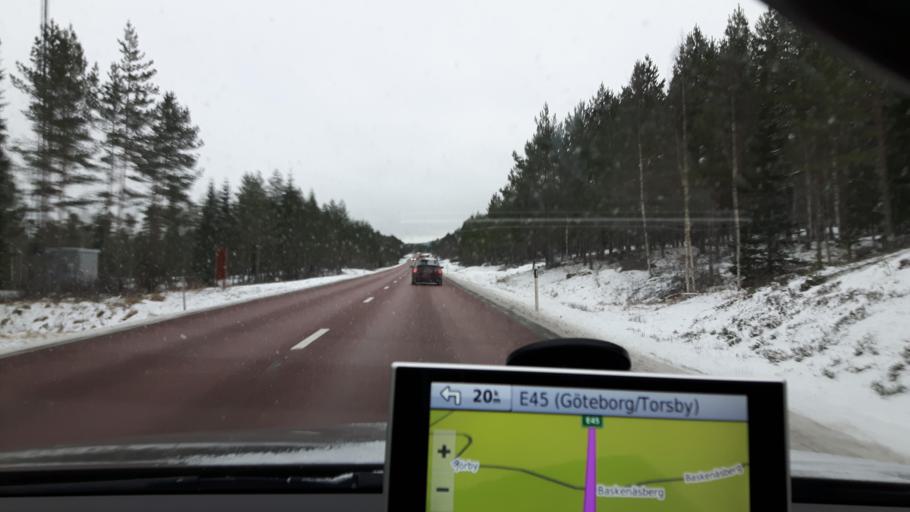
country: SE
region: Vaermland
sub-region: Hagfors Kommun
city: Ekshaerad
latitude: 60.4057
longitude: 13.2587
